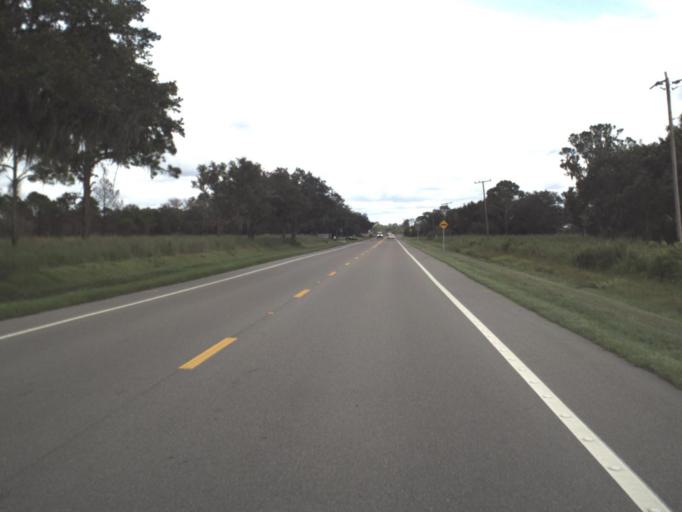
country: US
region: Florida
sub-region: Sarasota County
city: Lake Sarasota
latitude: 27.2440
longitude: -82.3463
